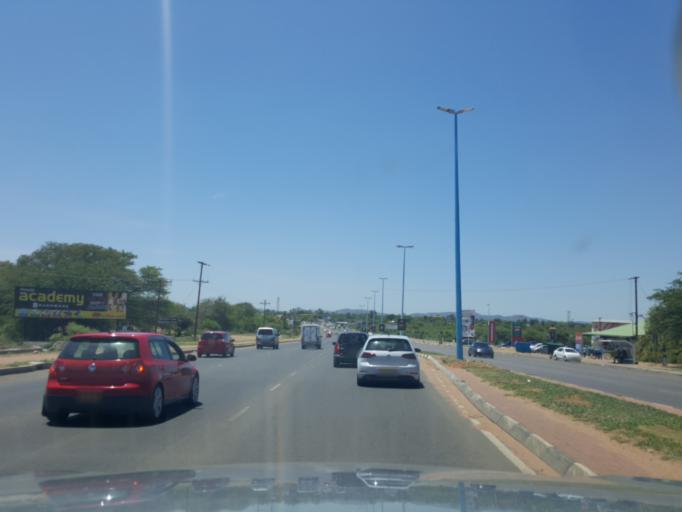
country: BW
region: Kweneng
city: Mogoditshane
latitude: -24.6393
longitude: 25.8802
